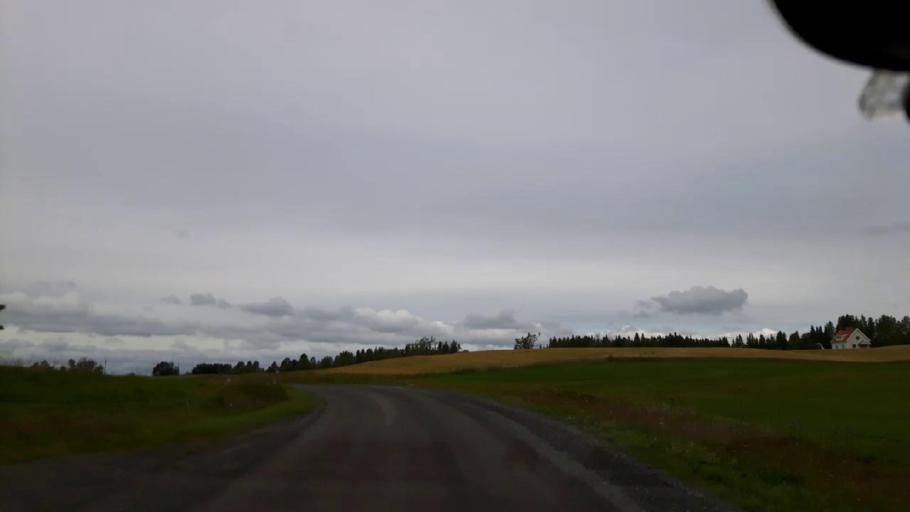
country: SE
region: Jaemtland
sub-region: Krokoms Kommun
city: Krokom
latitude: 63.3060
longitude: 14.3393
